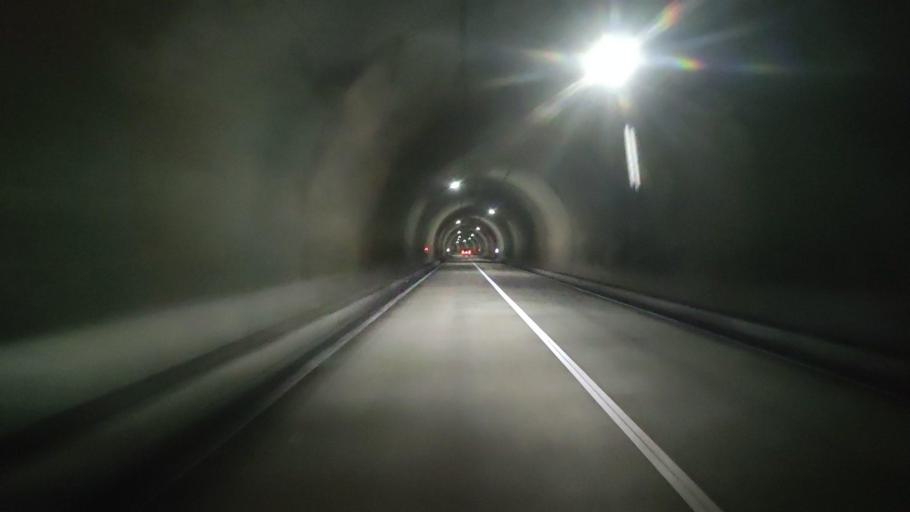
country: JP
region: Wakayama
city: Shingu
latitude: 33.8833
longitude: 135.8783
